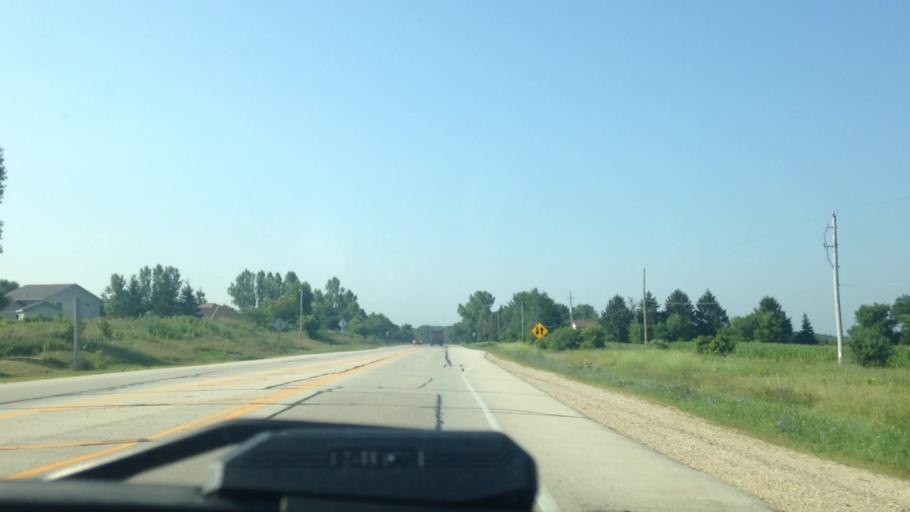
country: US
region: Wisconsin
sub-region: Waukesha County
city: Merton
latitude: 43.1916
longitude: -88.2615
